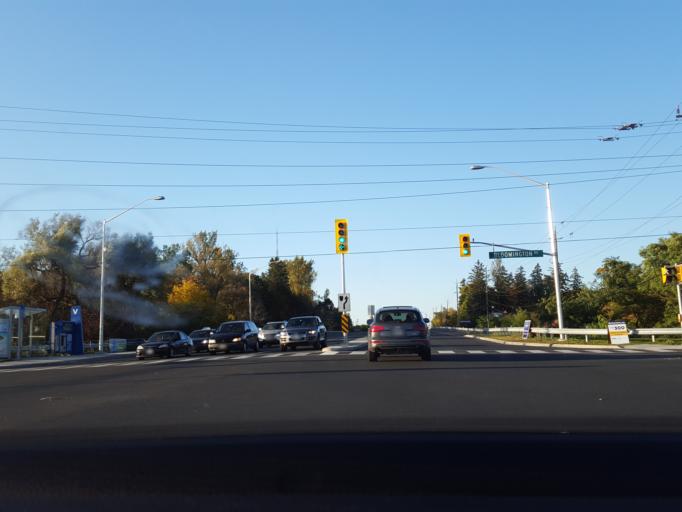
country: CA
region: Ontario
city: Newmarket
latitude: 43.9628
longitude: -79.4587
